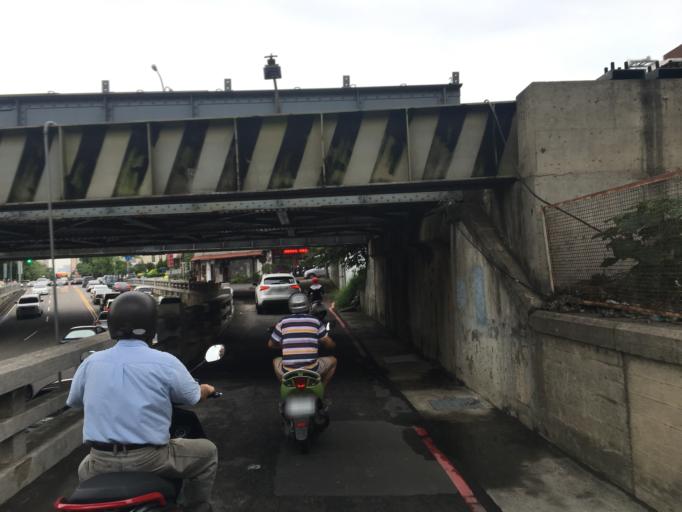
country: TW
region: Taiwan
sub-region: Taichung City
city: Taichung
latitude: 24.1327
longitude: 120.6763
